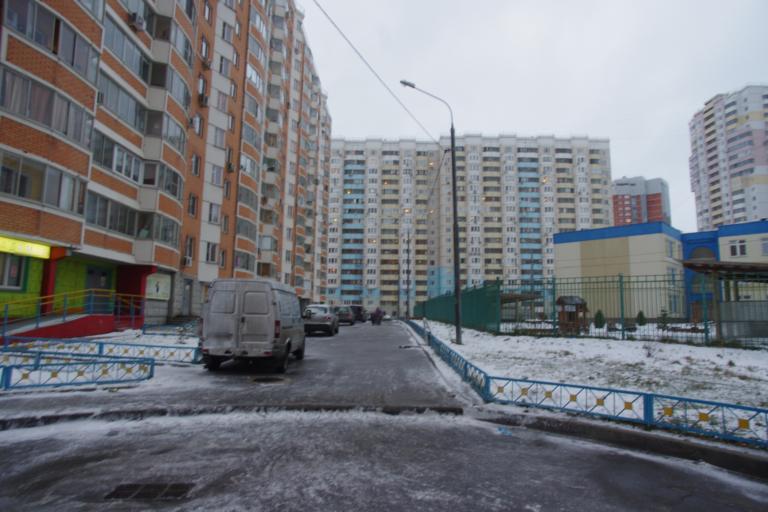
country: RU
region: Moskovskaya
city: Pavshino
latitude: 55.8214
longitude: 37.3655
